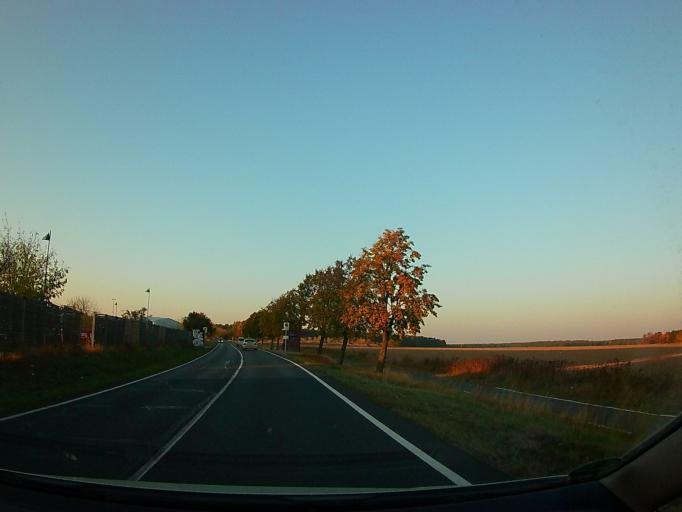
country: DE
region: Brandenburg
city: Schulzendorf
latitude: 52.3732
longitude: 13.5659
